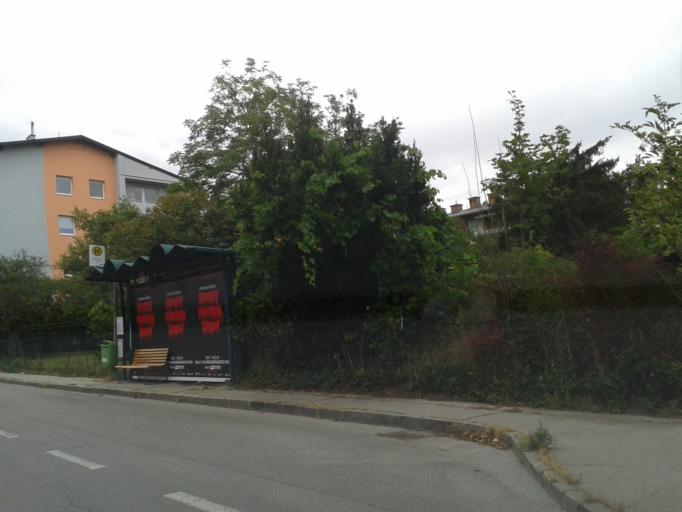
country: AT
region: Lower Austria
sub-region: Politischer Bezirk Modling
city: Perchtoldsdorf
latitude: 48.1248
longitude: 16.2700
